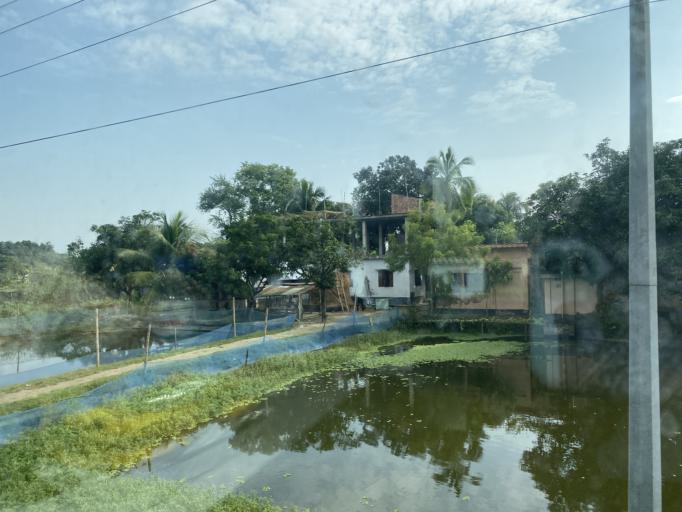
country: BD
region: Chittagong
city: Nabinagar
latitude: 23.9514
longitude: 91.1199
